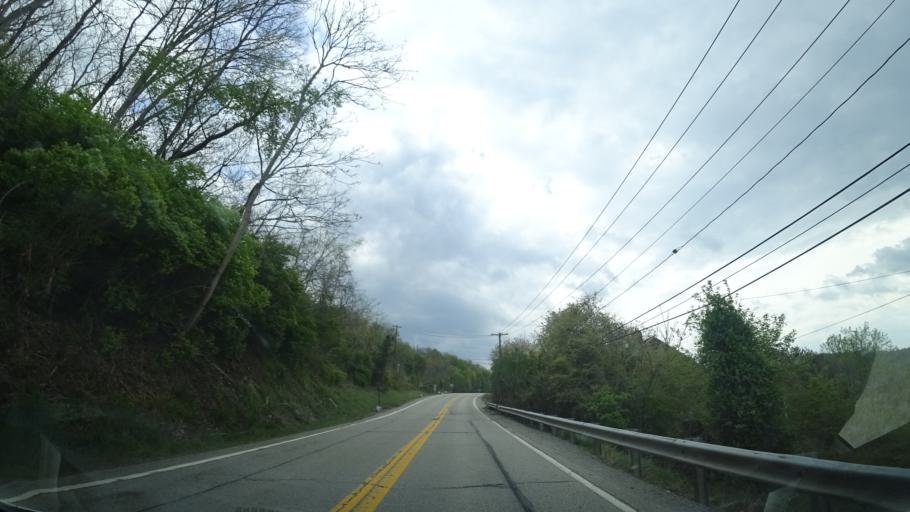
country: US
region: Pennsylvania
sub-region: Fayette County
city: Fairhope
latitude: 40.1083
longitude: -79.8423
